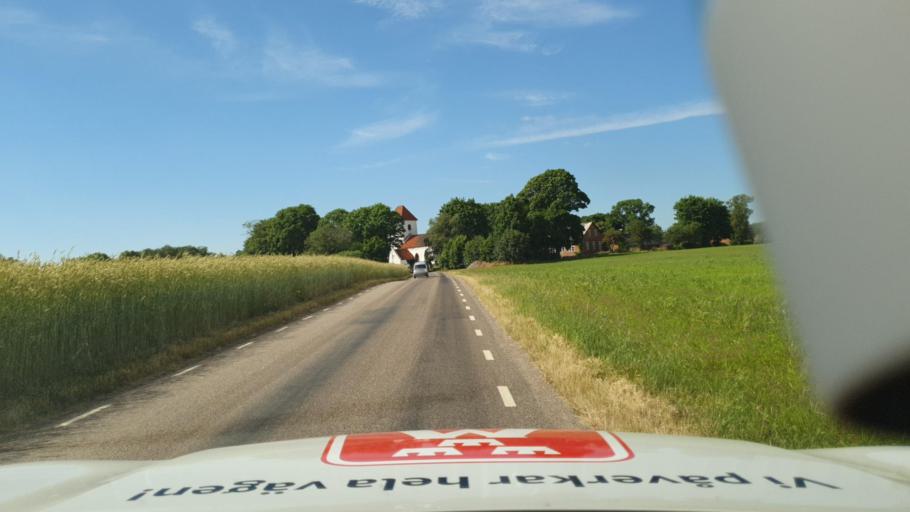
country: SE
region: Skane
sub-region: Sjobo Kommun
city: Blentarp
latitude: 55.6068
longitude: 13.5918
